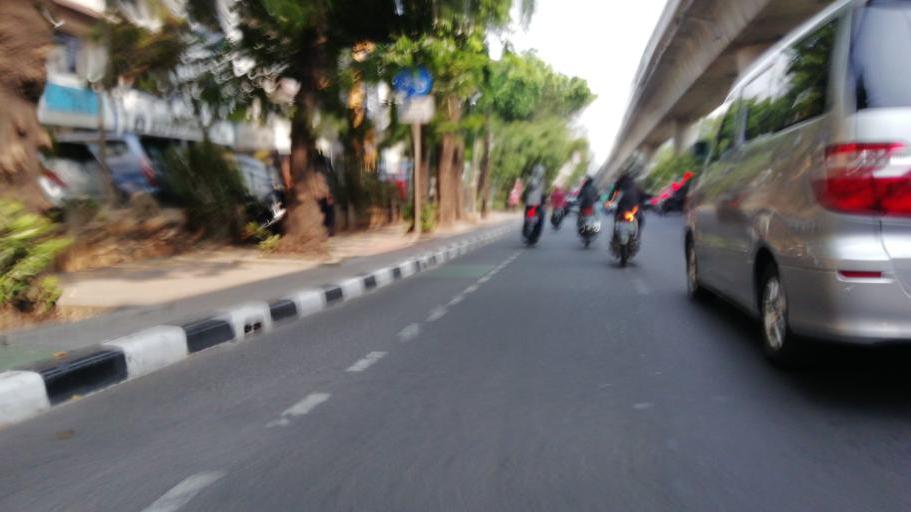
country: ID
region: Jakarta Raya
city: Jakarta
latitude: -6.2458
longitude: 106.8048
